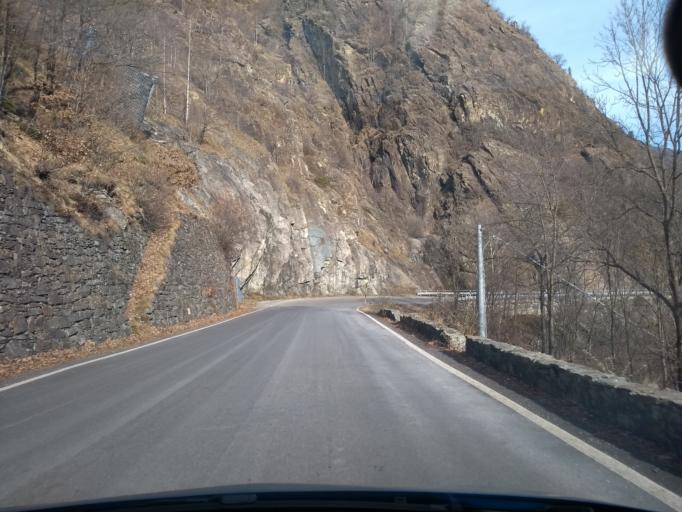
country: IT
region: Piedmont
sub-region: Provincia di Torino
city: Ala di Stura
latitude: 45.3189
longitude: 7.3349
